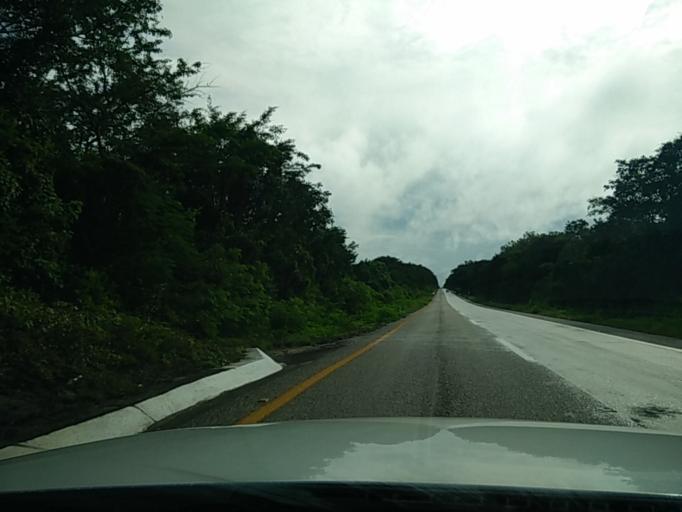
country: MX
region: Yucatan
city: Tunkas
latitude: 20.7589
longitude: -88.7675
